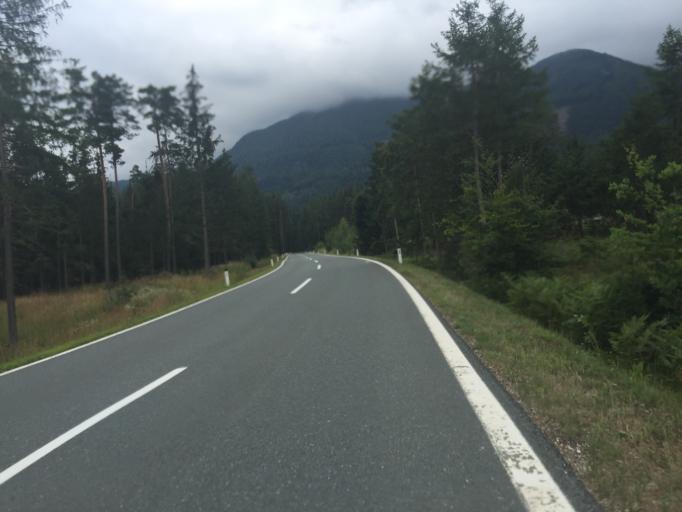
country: AT
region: Carinthia
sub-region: Politischer Bezirk Volkermarkt
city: Feistritz ob Bleiburg
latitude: 46.5508
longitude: 14.7699
